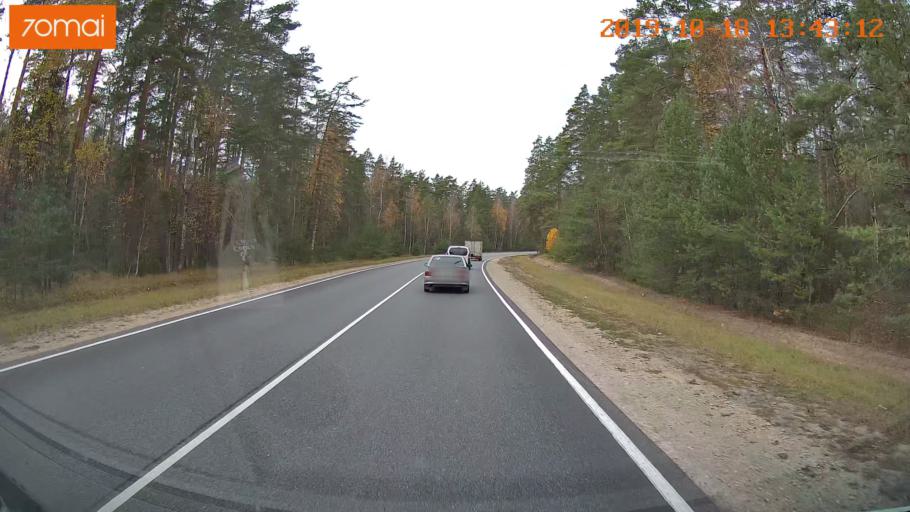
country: RU
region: Rjazan
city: Solotcha
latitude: 54.9288
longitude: 39.9775
